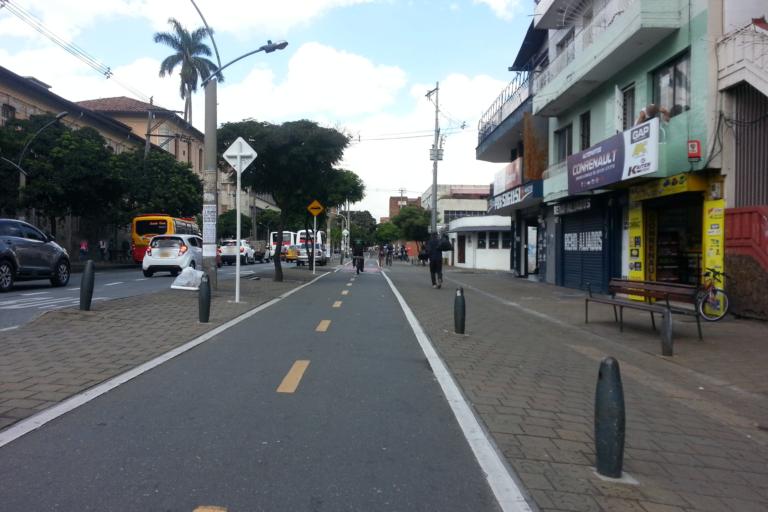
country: CO
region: Antioquia
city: Medellin
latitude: 6.2627
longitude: -75.5667
